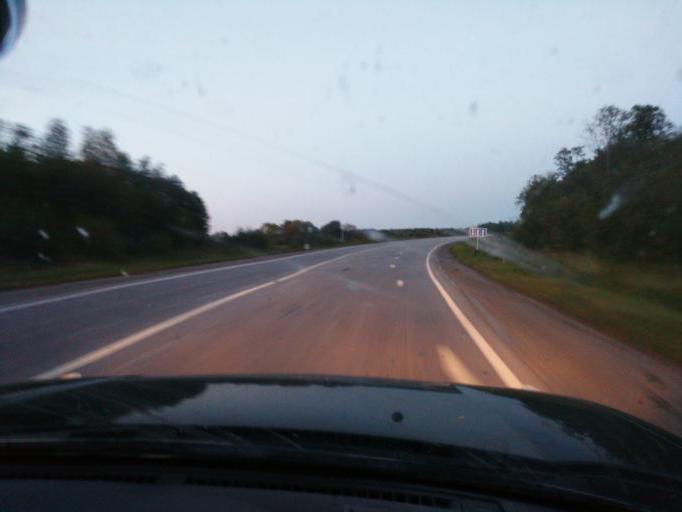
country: RU
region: Perm
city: Verkhnechusovskiye Gorodki
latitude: 58.2673
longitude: 57.3457
